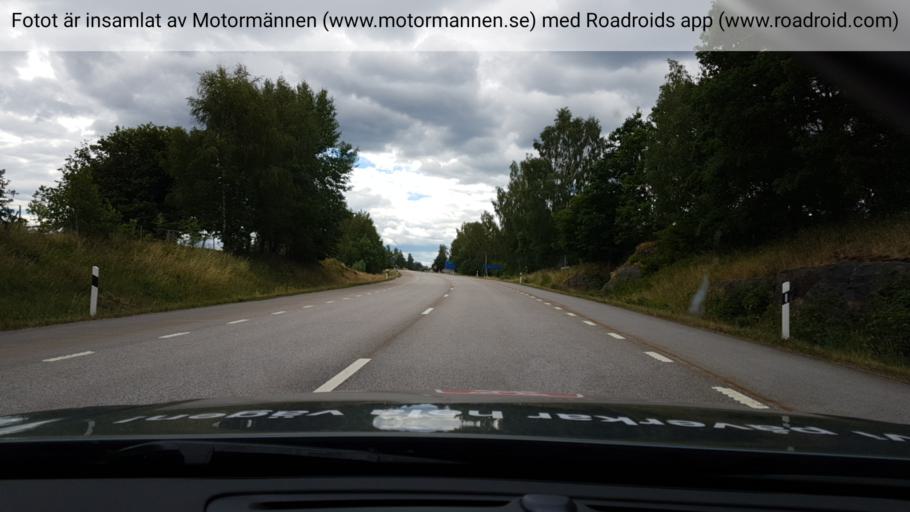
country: SE
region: Kalmar
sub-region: Vasterviks Kommun
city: Ankarsrum
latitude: 57.7179
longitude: 16.4504
